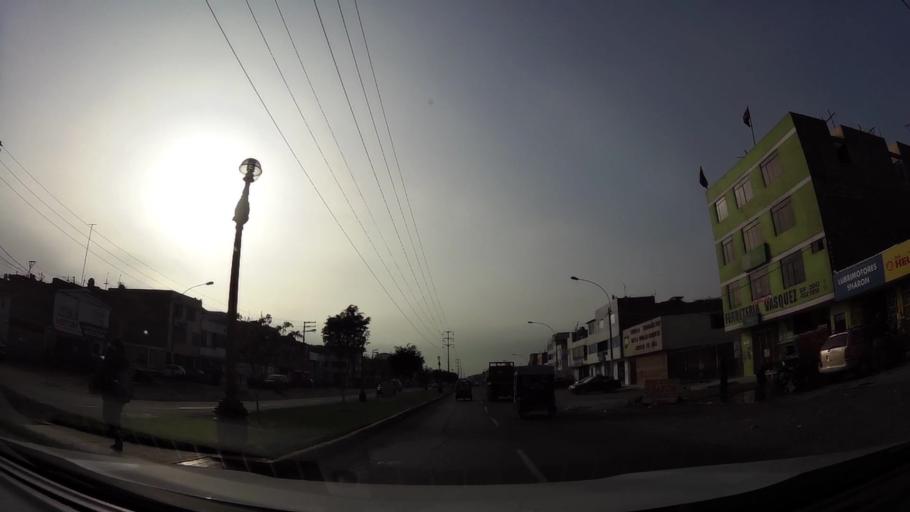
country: PE
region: Callao
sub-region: Callao
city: Callao
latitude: -12.0045
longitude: -77.0999
